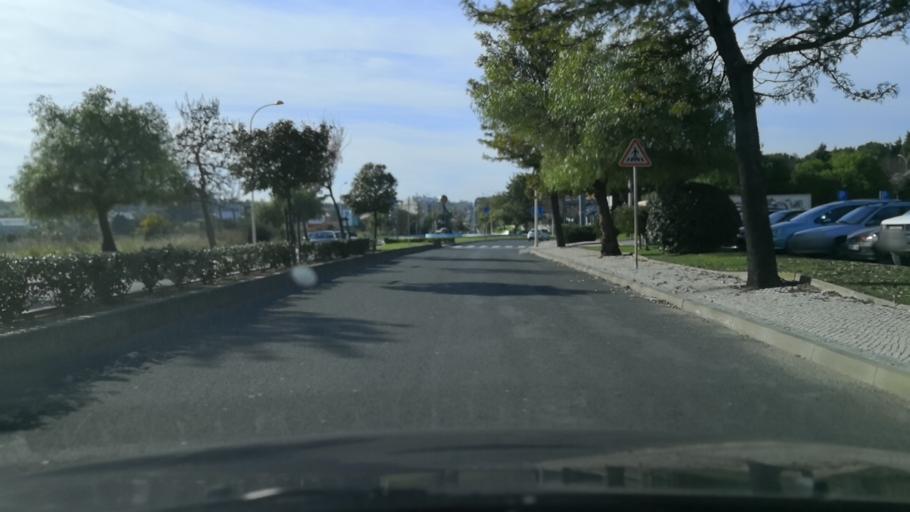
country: PT
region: Santarem
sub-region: Torres Novas
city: Torres Novas
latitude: 39.4707
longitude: -8.5393
